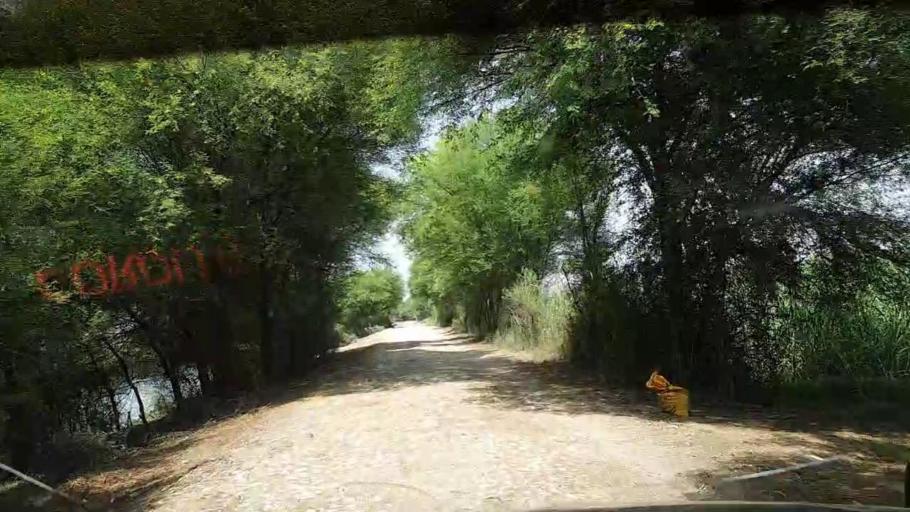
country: PK
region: Sindh
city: Ghotki
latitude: 28.0924
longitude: 69.3125
